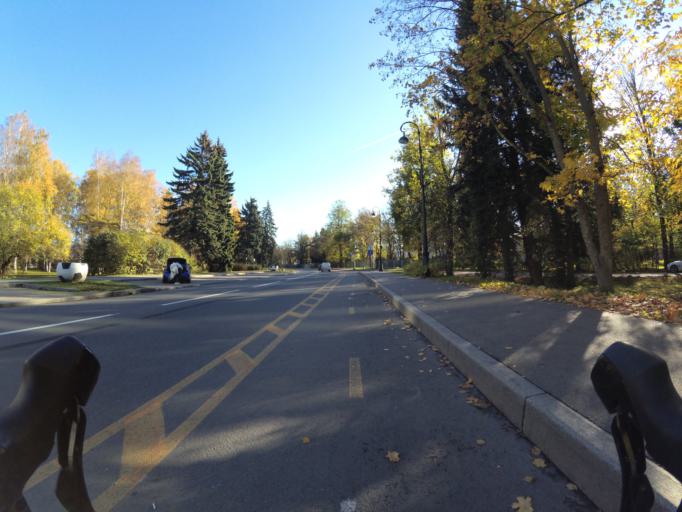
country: RU
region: Leningrad
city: Krestovskiy ostrov
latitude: 59.9742
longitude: 30.2490
